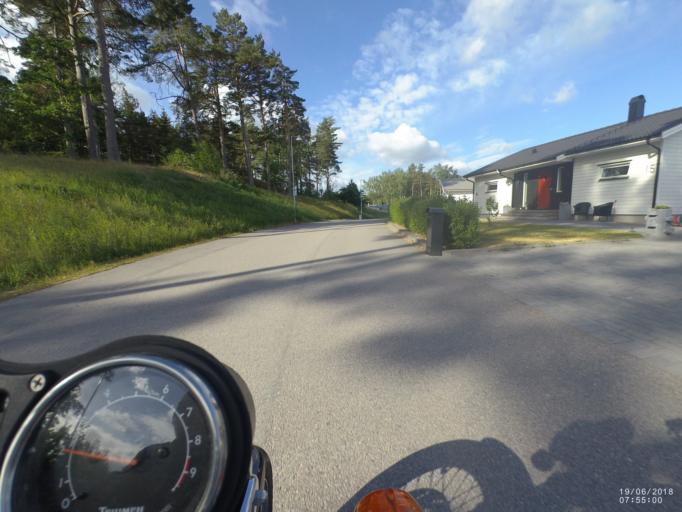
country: SE
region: Soedermanland
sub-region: Nykopings Kommun
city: Nykoping
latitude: 58.7775
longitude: 17.0098
